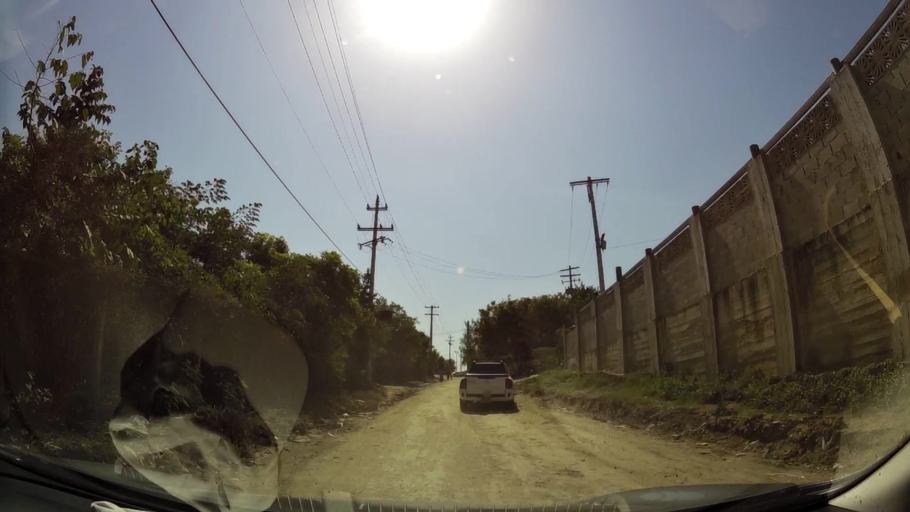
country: CO
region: Bolivar
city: Cartagena
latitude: 10.3635
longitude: -75.4897
